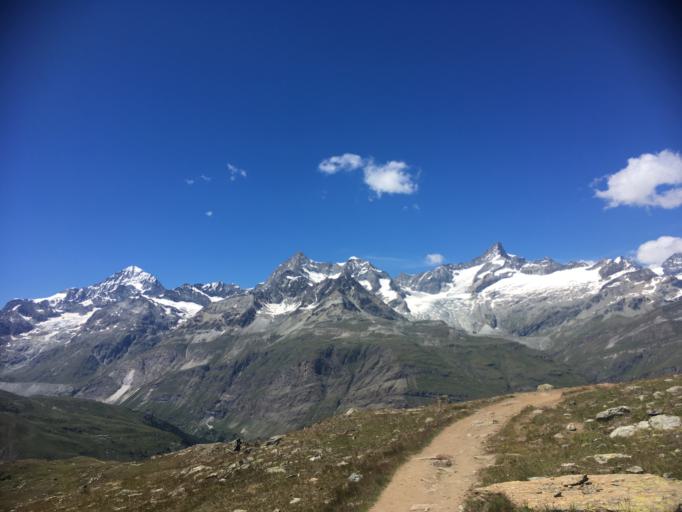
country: CH
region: Valais
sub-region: Visp District
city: Zermatt
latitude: 45.9863
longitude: 7.7516
